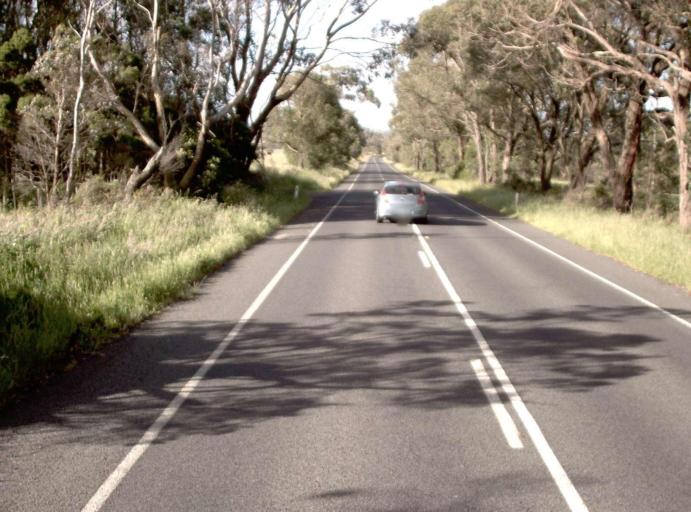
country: AU
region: Victoria
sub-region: Bass Coast
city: North Wonthaggi
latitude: -38.5575
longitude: 145.8433
